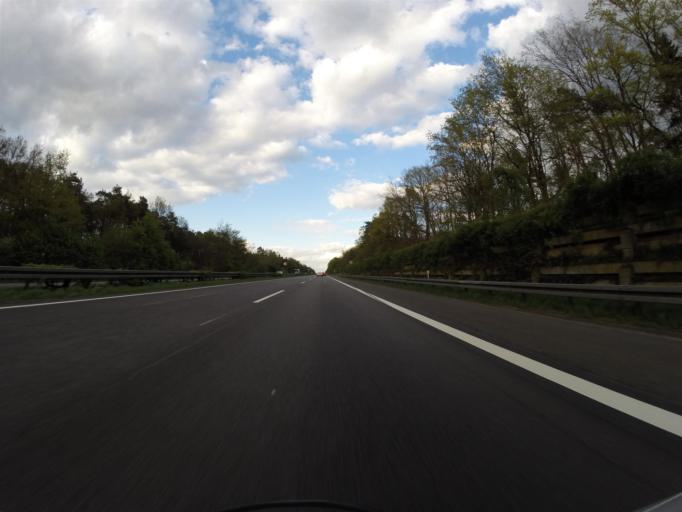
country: DE
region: Rheinland-Pfalz
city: Waldmohr
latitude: 49.3552
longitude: 7.3270
